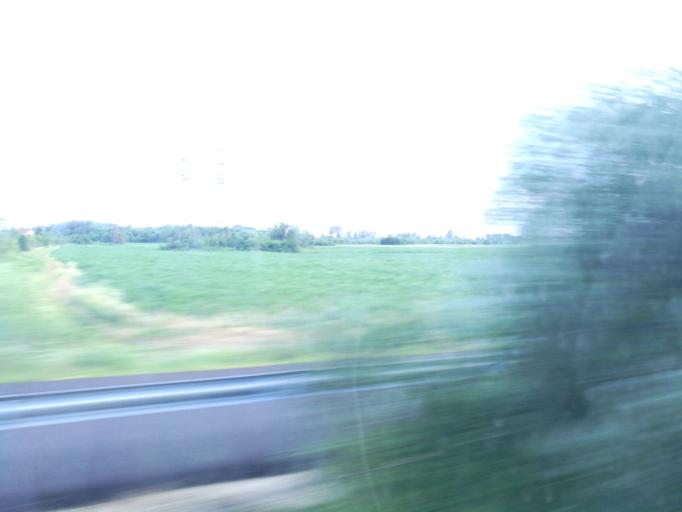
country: RO
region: Dambovita
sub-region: Comuna Branistea
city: Dambovicioara
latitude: 44.6631
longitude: 25.5539
